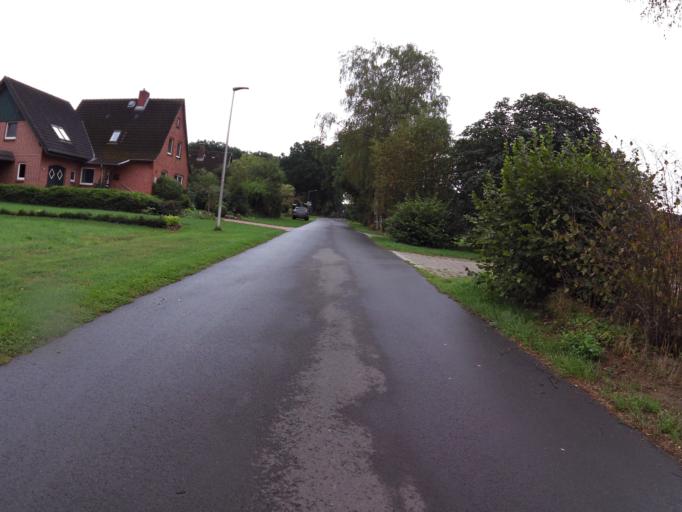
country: DE
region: Lower Saxony
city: Hamersen
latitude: 53.2576
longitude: 9.4791
